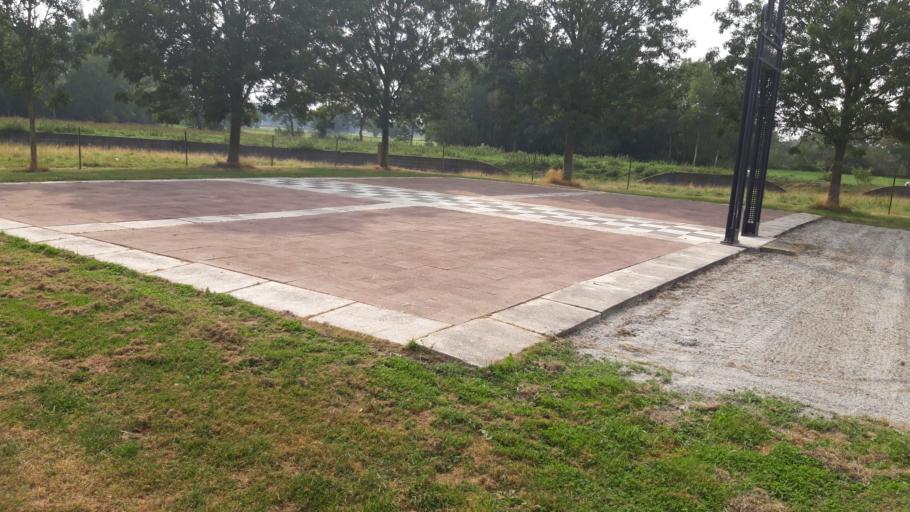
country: NL
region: Drenthe
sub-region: Gemeente Tynaarlo
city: Vries
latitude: 53.1268
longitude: 6.5654
